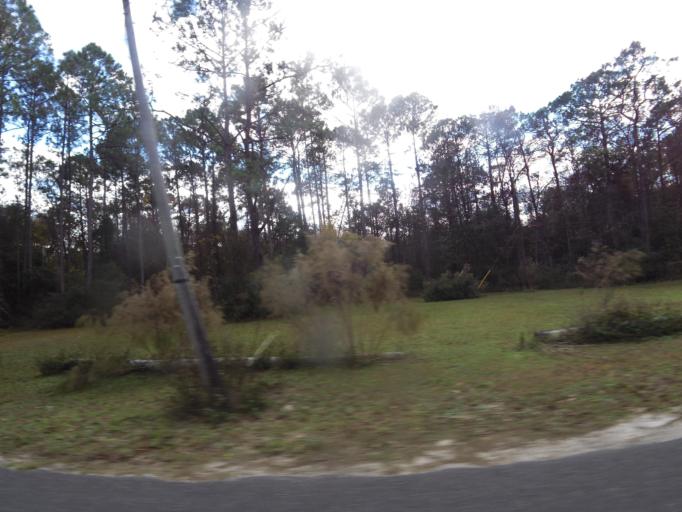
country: US
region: Florida
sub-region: Clay County
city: Middleburg
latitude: 30.1208
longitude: -81.9332
